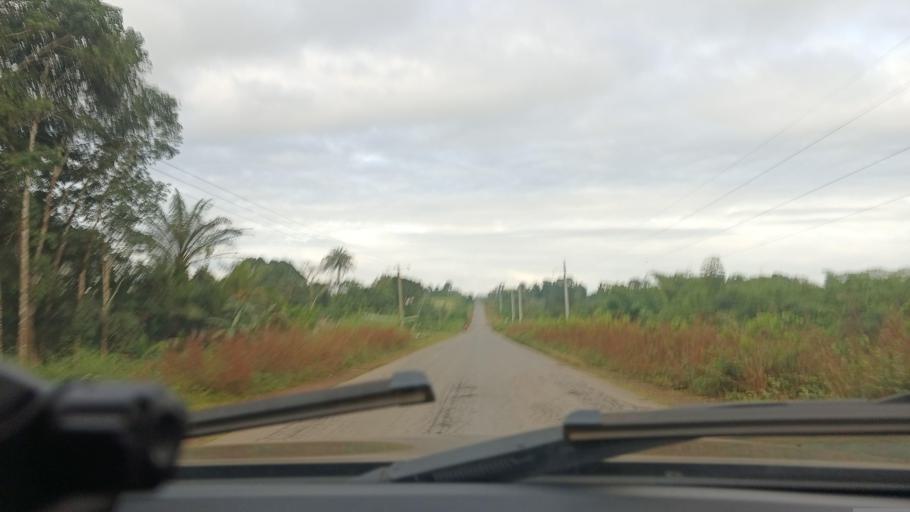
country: LR
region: Montserrado
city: Monrovia
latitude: 6.5465
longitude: -10.8606
